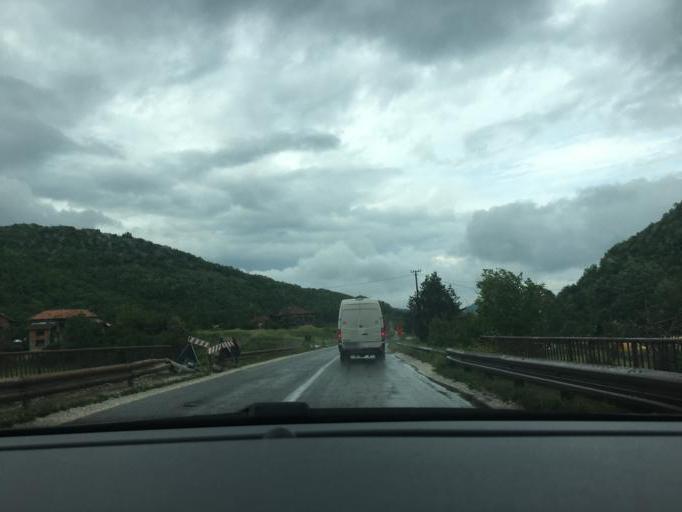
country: MK
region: Debarca
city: Belcista
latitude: 41.3247
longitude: 20.7927
